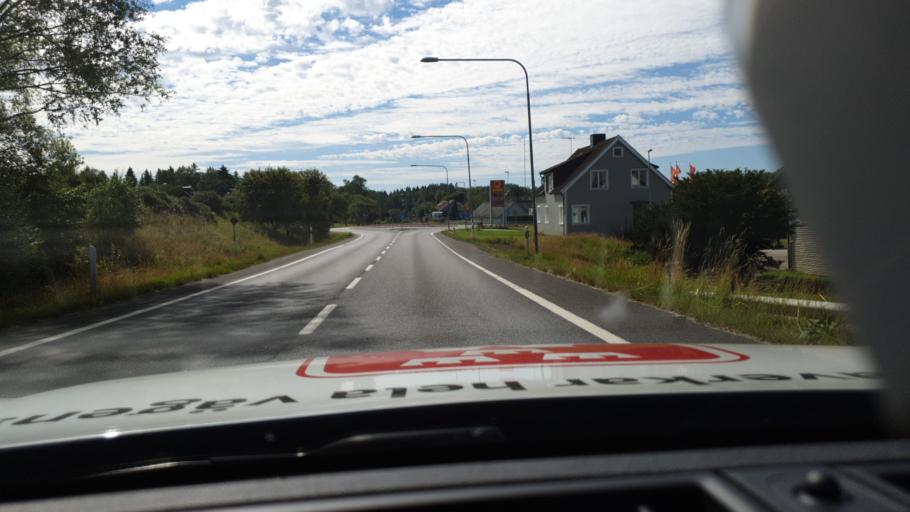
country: SE
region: Joenkoeping
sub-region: Vaggeryds Kommun
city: Vaggeryd
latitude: 57.5137
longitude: 14.2793
